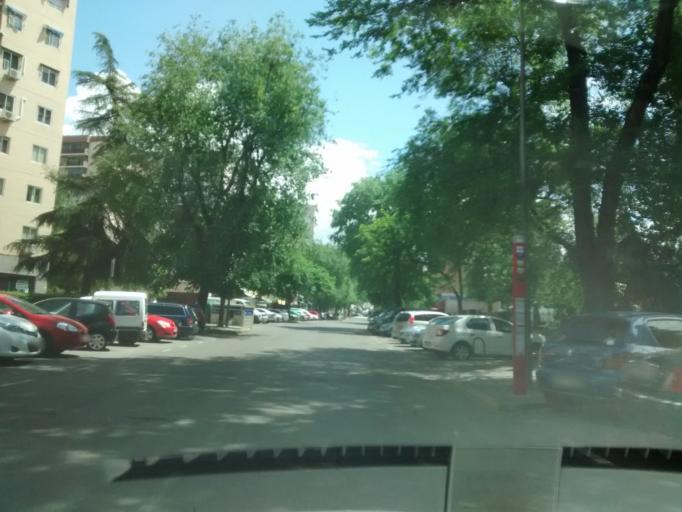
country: ES
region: Madrid
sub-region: Provincia de Madrid
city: San Fernando de Henares
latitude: 40.4296
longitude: -3.5413
